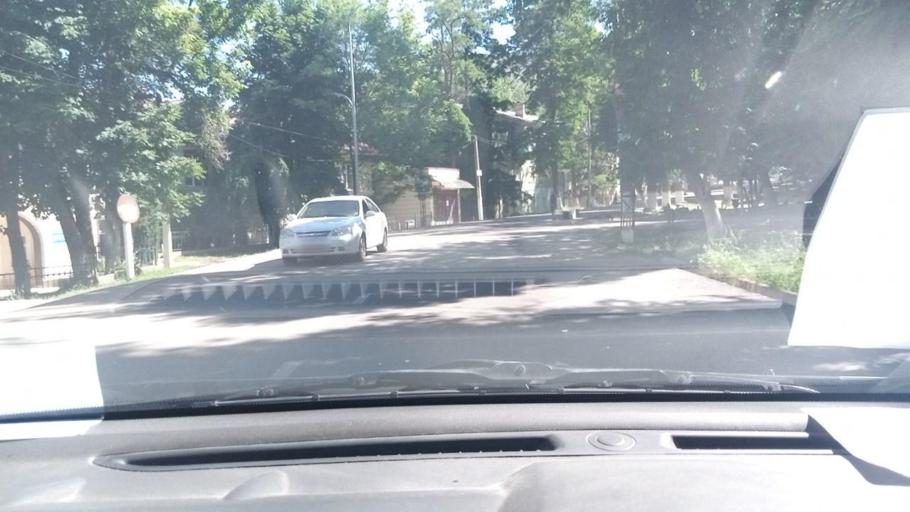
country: UZ
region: Toshkent
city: Yangiobod
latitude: 41.1181
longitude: 70.0912
